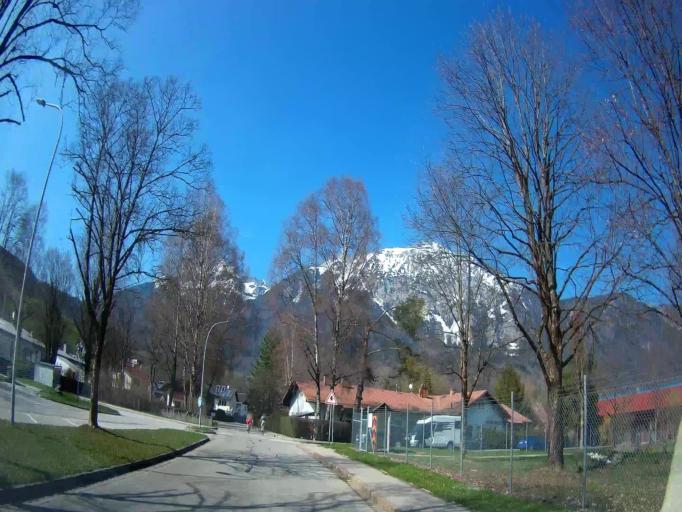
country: DE
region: Bavaria
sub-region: Upper Bavaria
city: Bad Reichenhall
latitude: 47.7251
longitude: 12.8572
